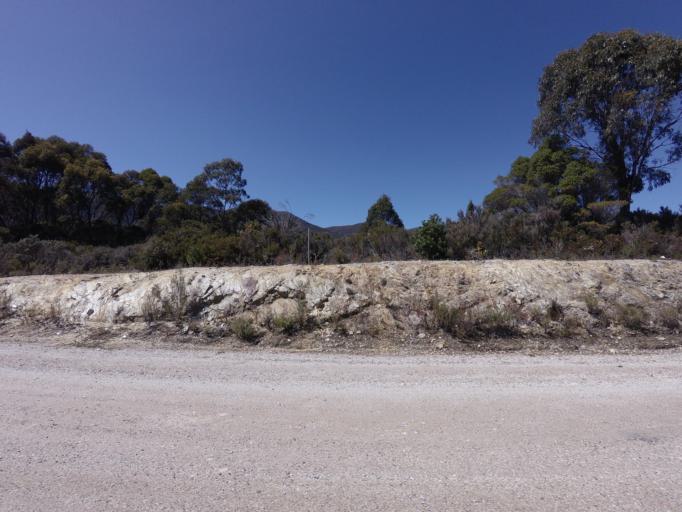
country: AU
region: Tasmania
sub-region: Huon Valley
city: Geeveston
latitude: -43.0279
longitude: 146.3521
